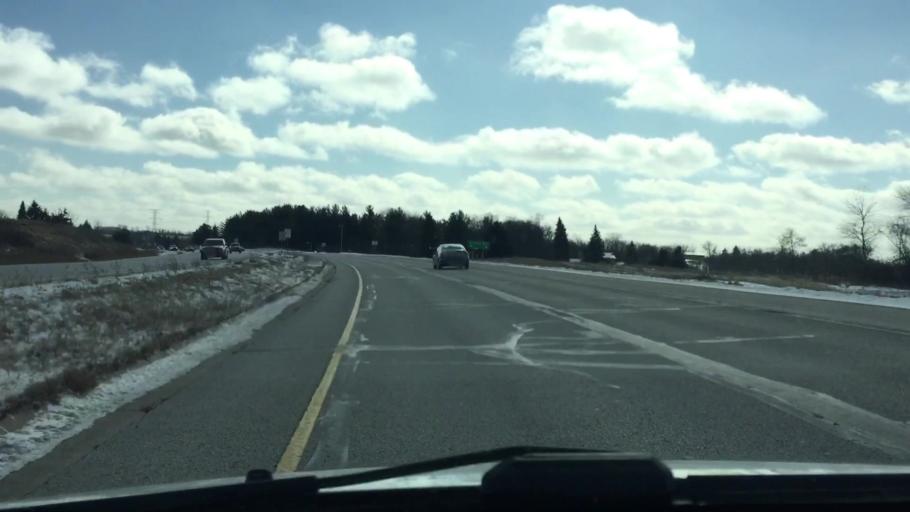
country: US
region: Wisconsin
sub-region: Waukesha County
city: Big Bend
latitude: 42.9249
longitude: -88.2287
